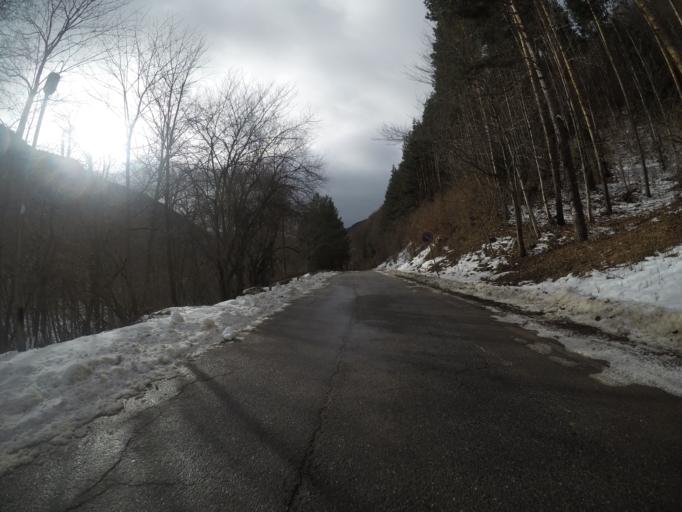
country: BG
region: Kyustendil
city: Sapareva Banya
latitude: 42.1401
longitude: 23.3488
